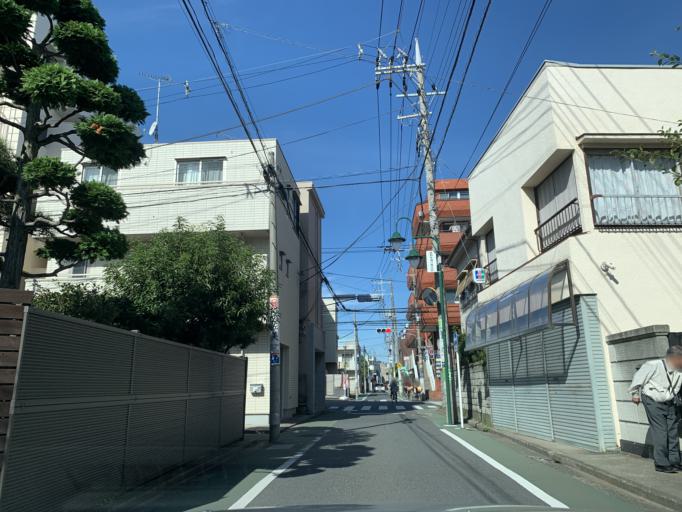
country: JP
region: Chiba
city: Matsudo
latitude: 35.7272
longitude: 139.9273
